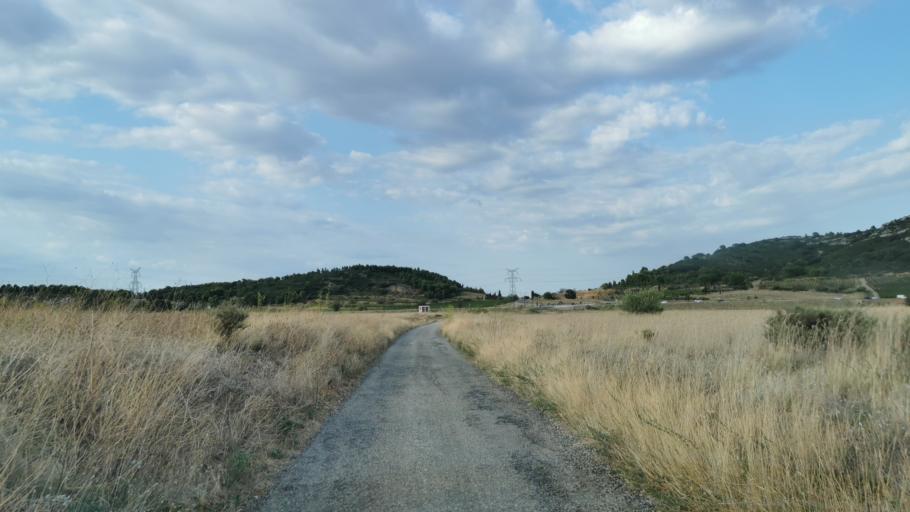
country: FR
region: Languedoc-Roussillon
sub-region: Departement de l'Aude
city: Nevian
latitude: 43.1943
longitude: 2.8956
